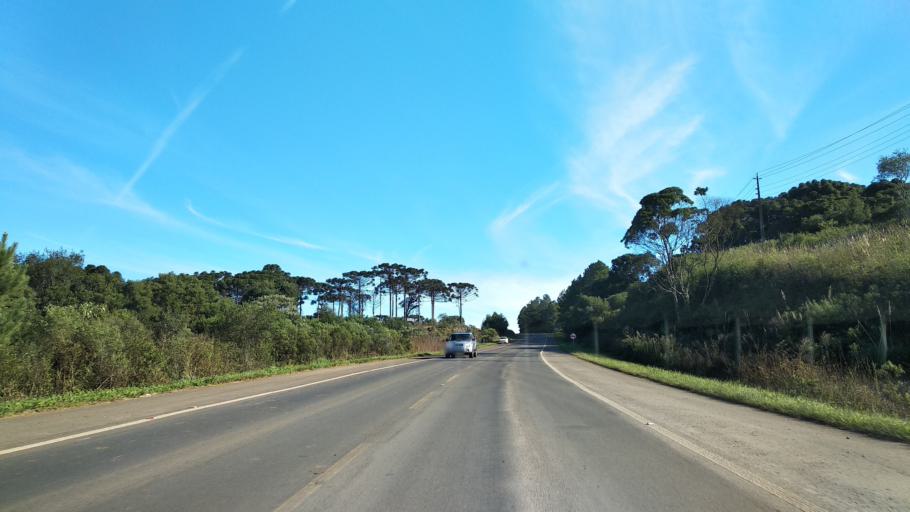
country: BR
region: Santa Catarina
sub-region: Campos Novos
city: Campos Novos
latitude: -27.4037
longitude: -51.2047
